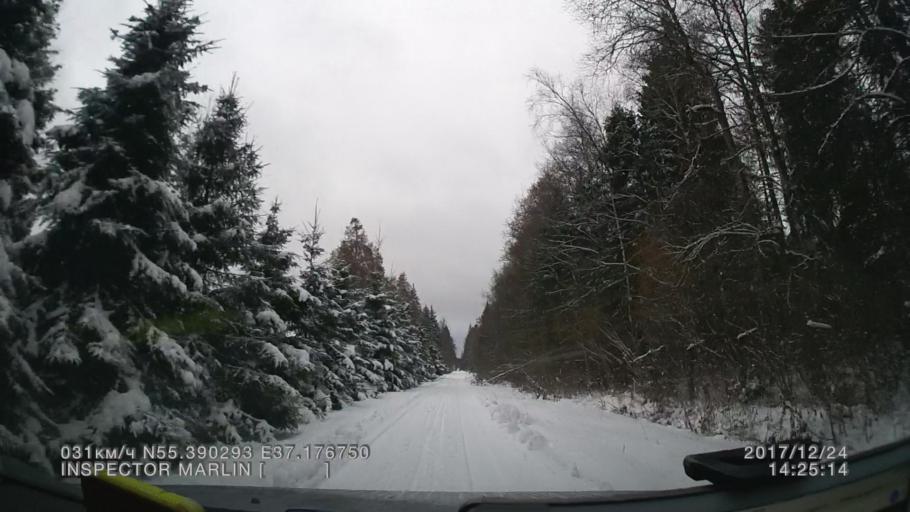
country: RU
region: Moskovskaya
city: Troitsk
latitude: 55.3902
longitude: 37.1766
